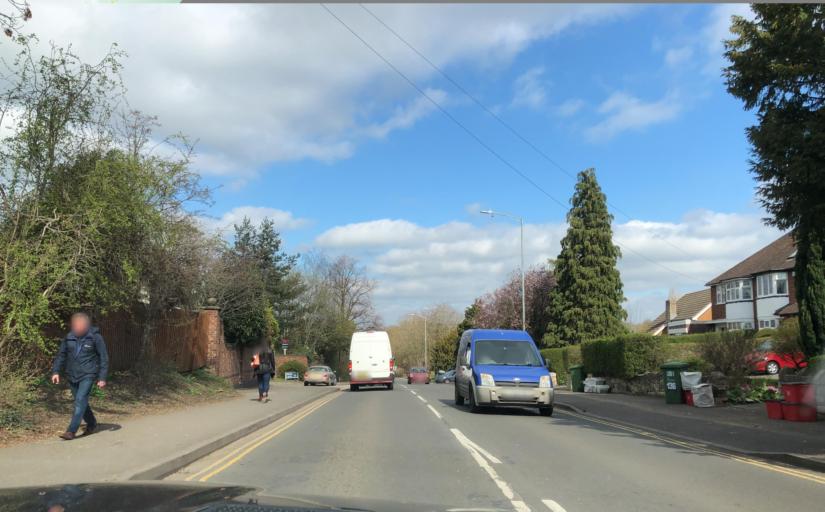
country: GB
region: England
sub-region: Warwickshire
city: Warwick
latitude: 52.2900
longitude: -1.5785
